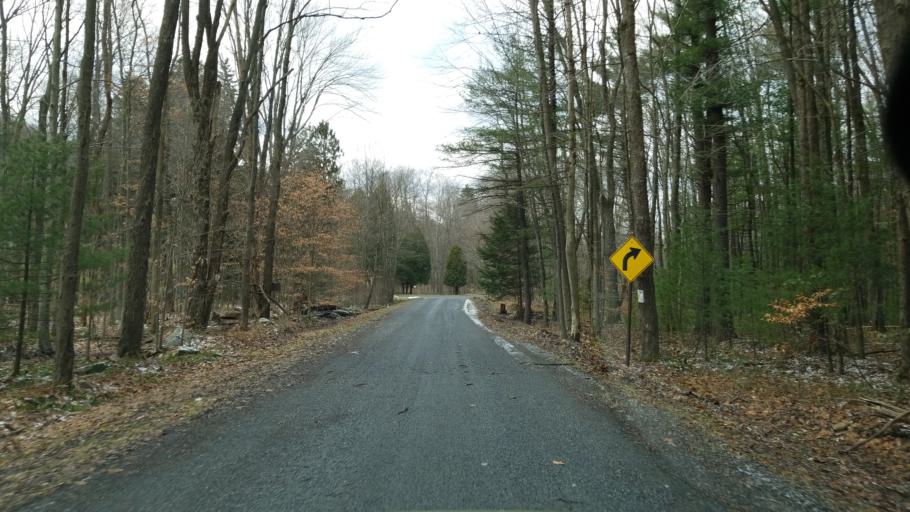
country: US
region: Pennsylvania
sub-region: Clearfield County
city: Clearfield
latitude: 41.1412
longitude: -78.5449
